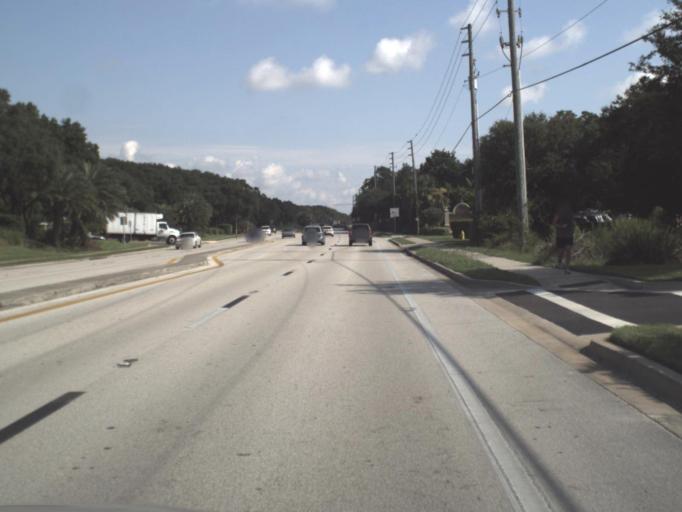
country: US
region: Florida
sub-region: Saint Johns County
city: Saint Augustine Beach
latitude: 29.8306
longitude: -81.2731
